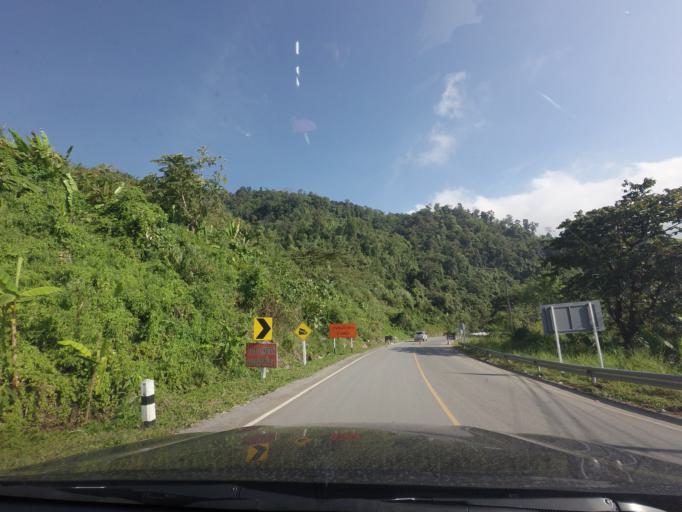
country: TH
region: Phetchabun
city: Lom Kao
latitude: 16.8866
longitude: 101.1203
